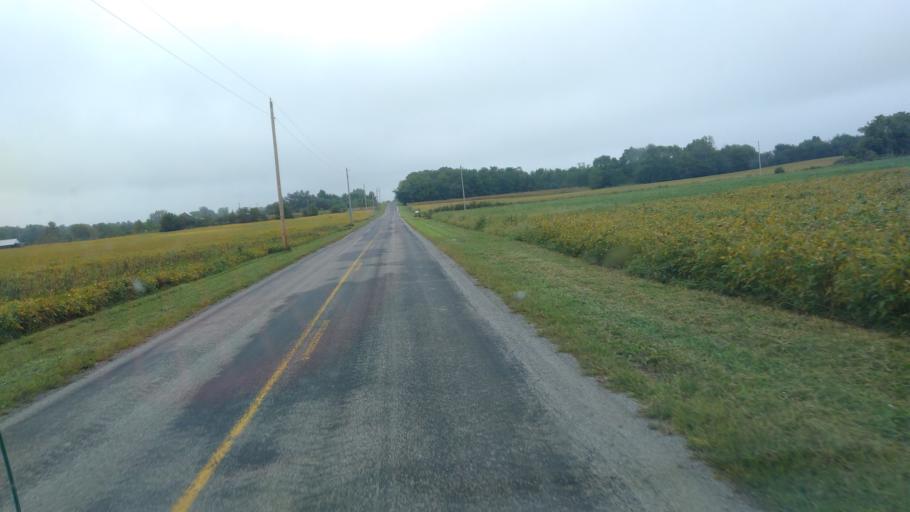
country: US
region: Ohio
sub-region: Hardin County
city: Kenton
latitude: 40.5654
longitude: -83.6367
